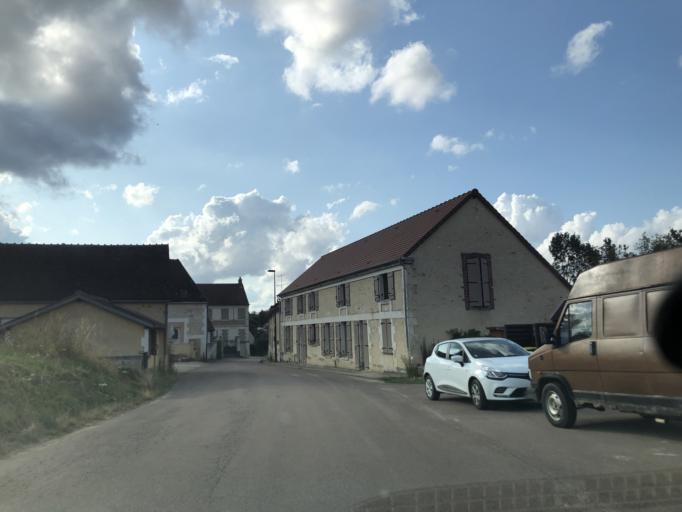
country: FR
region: Bourgogne
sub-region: Departement de l'Yonne
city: Charbuy
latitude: 47.8248
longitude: 3.4594
